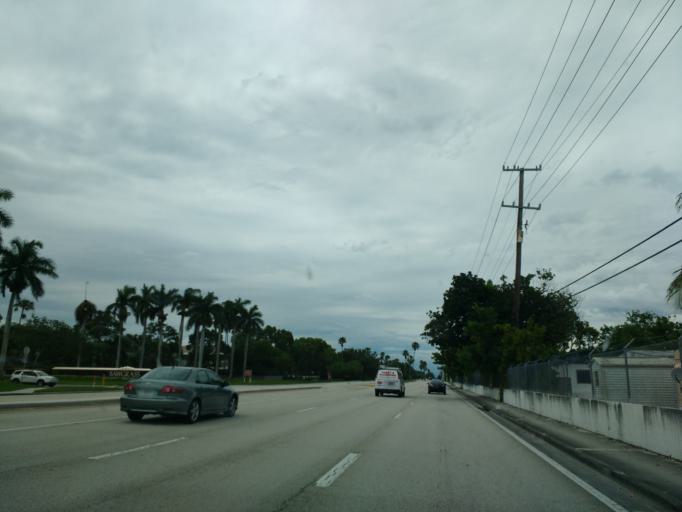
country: US
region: Florida
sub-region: Broward County
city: Pine Island Ridge
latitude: 26.1252
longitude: -80.3300
